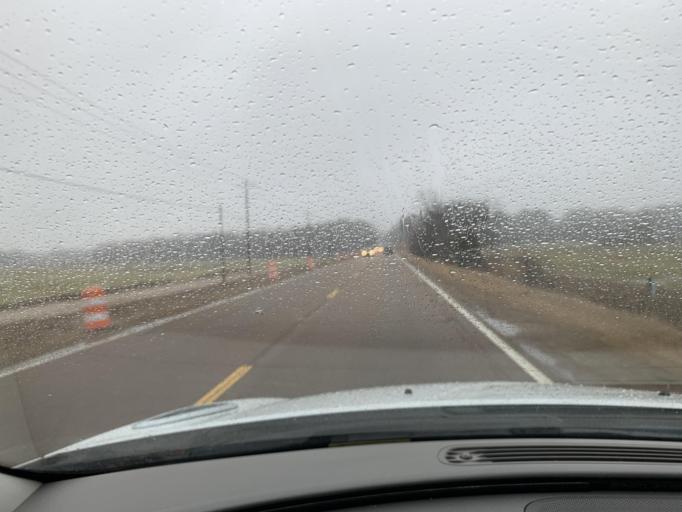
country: US
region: Mississippi
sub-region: De Soto County
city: Hernando
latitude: 34.8692
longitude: -89.9954
